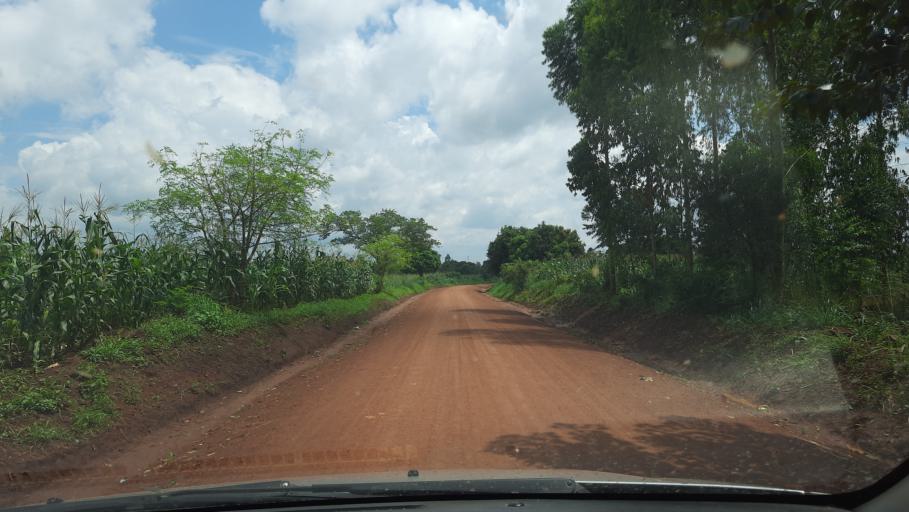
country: UG
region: Western Region
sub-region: Kiryandongo District
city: Kiryandongo
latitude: 1.8168
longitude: 31.9905
